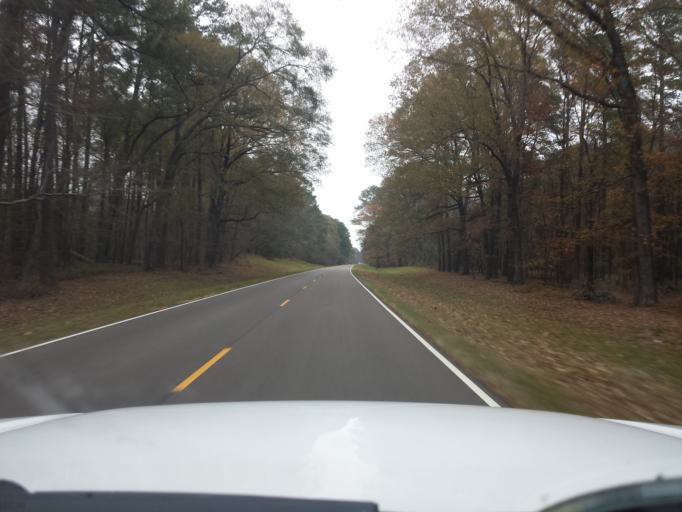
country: US
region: Mississippi
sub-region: Madison County
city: Canton
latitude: 32.5392
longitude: -89.9550
